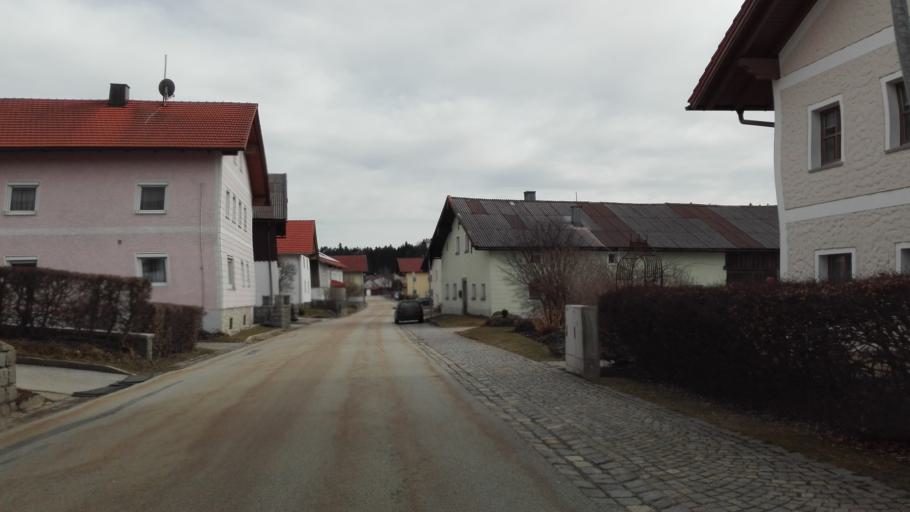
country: DE
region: Bavaria
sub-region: Lower Bavaria
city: Wegscheid
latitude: 48.6205
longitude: 13.7781
